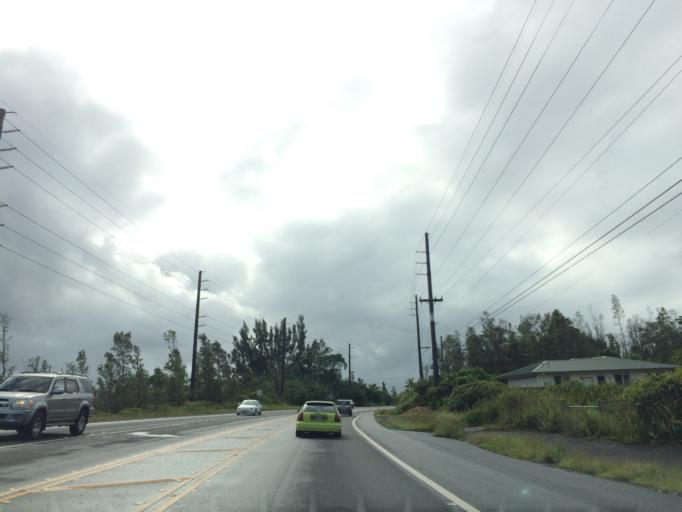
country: US
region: Hawaii
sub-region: Hawaii County
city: Ainaloa
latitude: 19.5427
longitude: -154.9744
